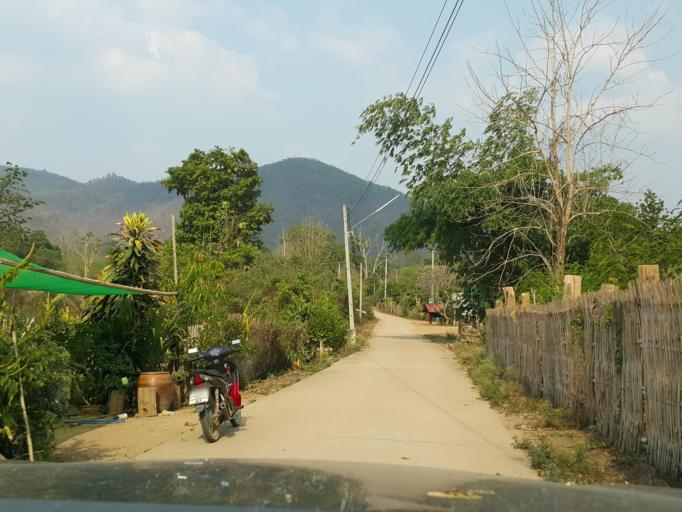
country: TH
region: Lamphun
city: Li
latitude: 17.6052
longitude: 98.9656
